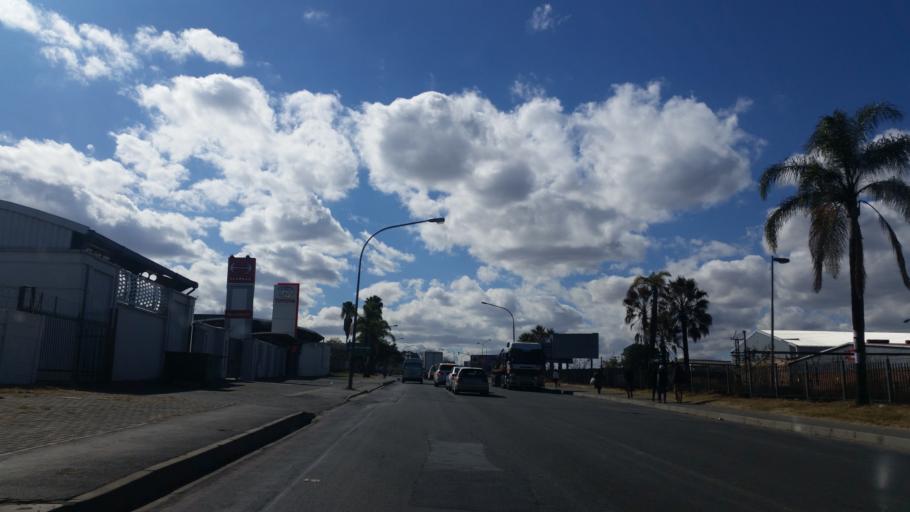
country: ZA
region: KwaZulu-Natal
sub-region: uThukela District Municipality
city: Ladysmith
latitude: -28.5551
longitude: 29.7856
